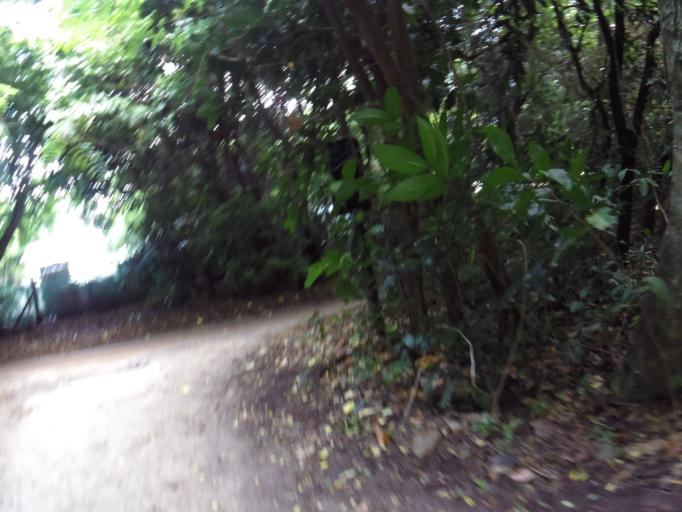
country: AU
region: Queensland
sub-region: Cairns
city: Yorkeys Knob
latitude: -16.7583
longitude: 145.9732
